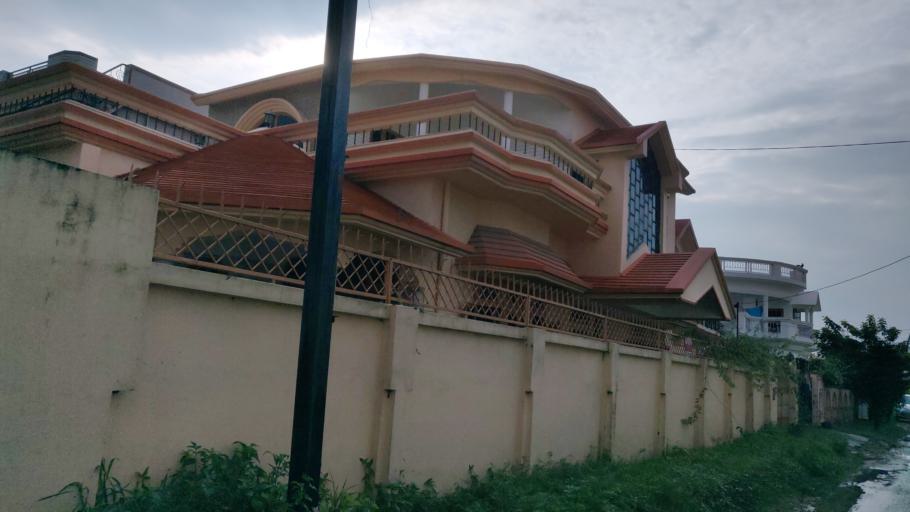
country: IN
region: Uttarakhand
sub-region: Dehradun
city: Dehradun
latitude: 30.3299
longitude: 78.0078
